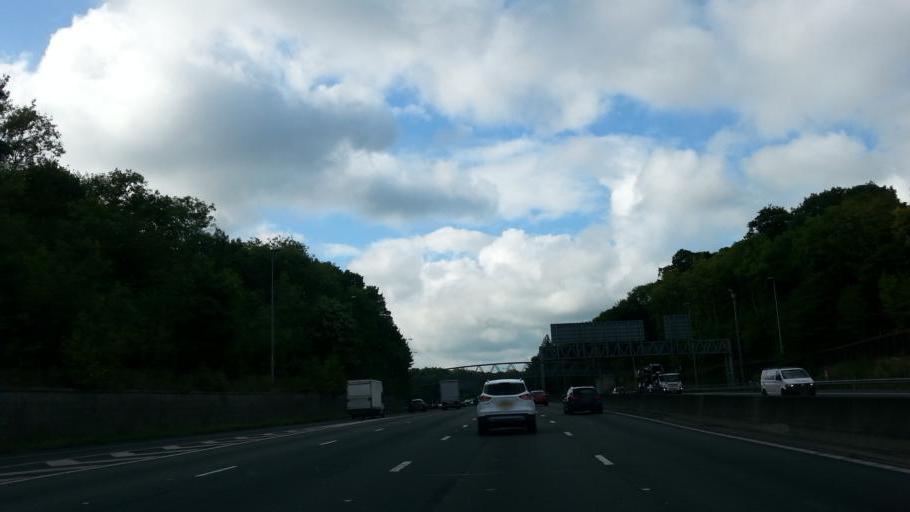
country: GB
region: England
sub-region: Hertfordshire
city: Chorleywood
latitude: 51.6538
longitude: -0.4960
